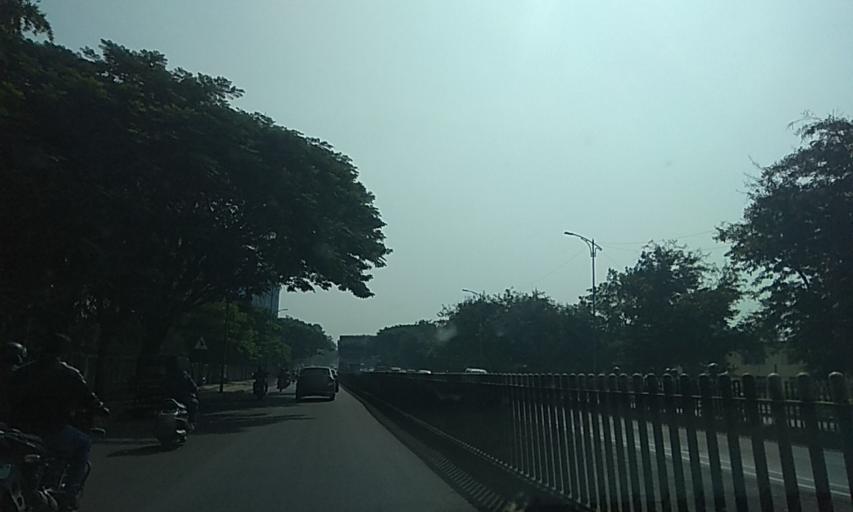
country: IN
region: Maharashtra
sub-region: Pune Division
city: Shivaji Nagar
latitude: 18.5463
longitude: 73.8750
